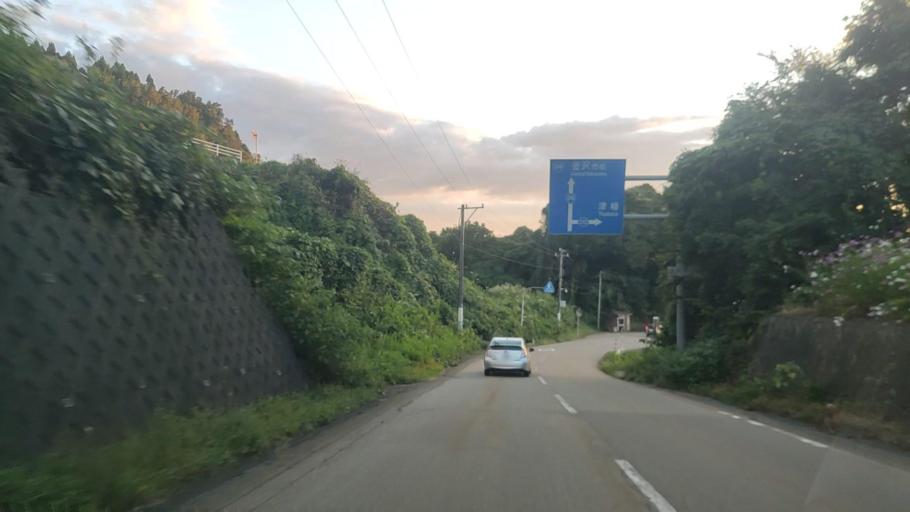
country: JP
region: Ishikawa
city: Tsubata
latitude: 36.6202
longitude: 136.7815
